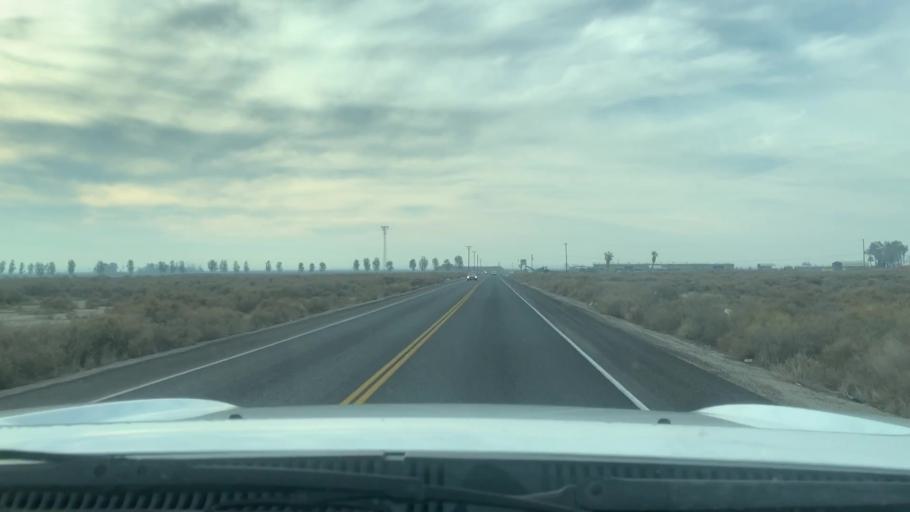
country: US
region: California
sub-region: Kern County
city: Buttonwillow
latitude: 35.4998
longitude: -119.5402
